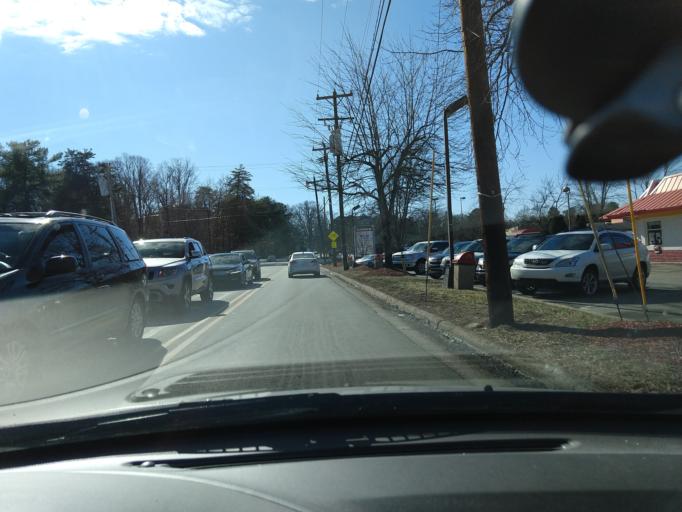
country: US
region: North Carolina
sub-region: Guilford County
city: Greensboro
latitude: 36.1206
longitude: -79.8431
